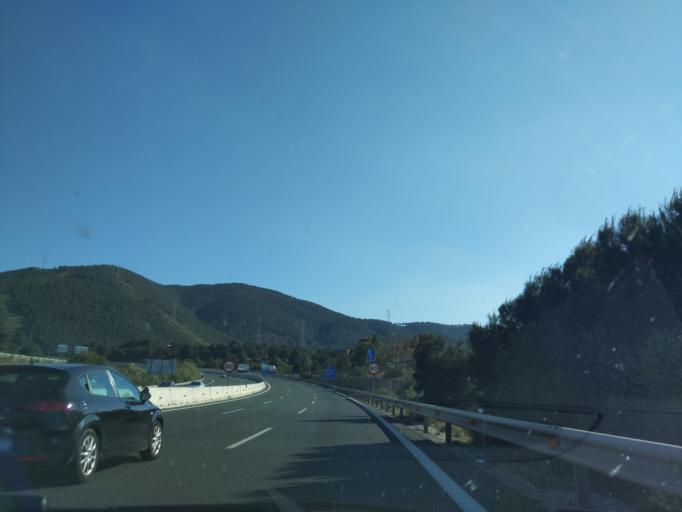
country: ES
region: Murcia
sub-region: Murcia
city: Alcantarilla
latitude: 37.9165
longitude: -1.1648
